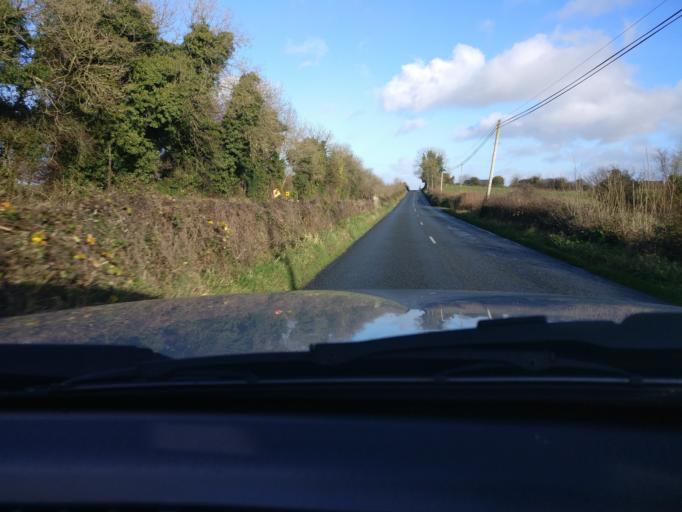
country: IE
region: Leinster
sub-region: An Iarmhi
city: Kilbeggan
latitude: 53.4524
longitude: -7.5267
